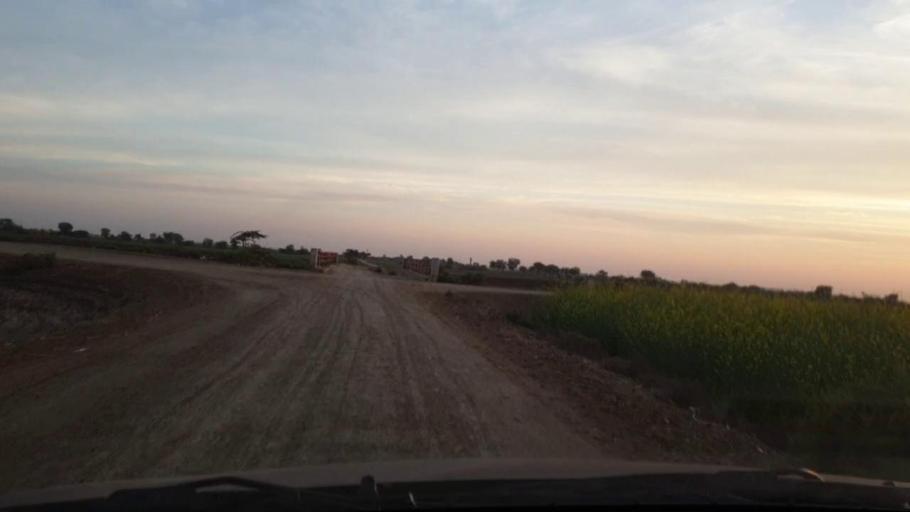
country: PK
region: Sindh
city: Sinjhoro
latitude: 26.0924
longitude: 68.7971
